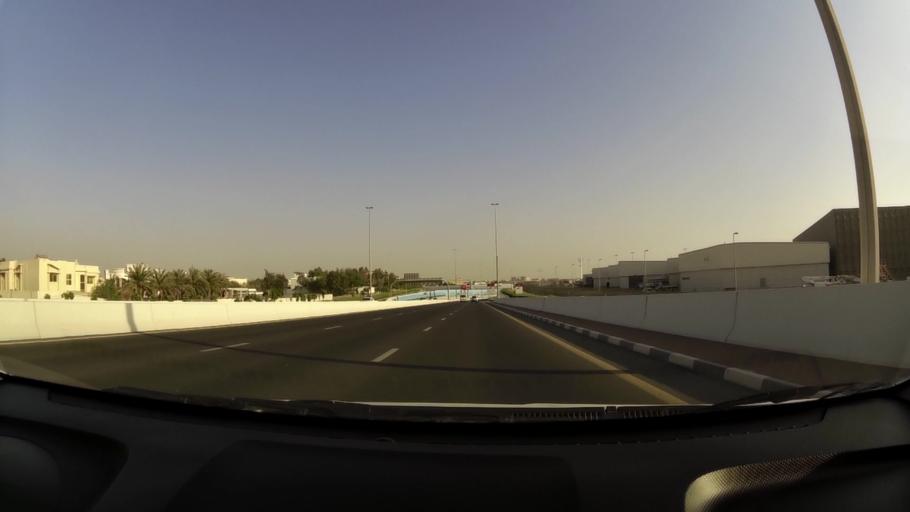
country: AE
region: Ash Shariqah
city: Sharjah
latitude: 25.2514
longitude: 55.3870
